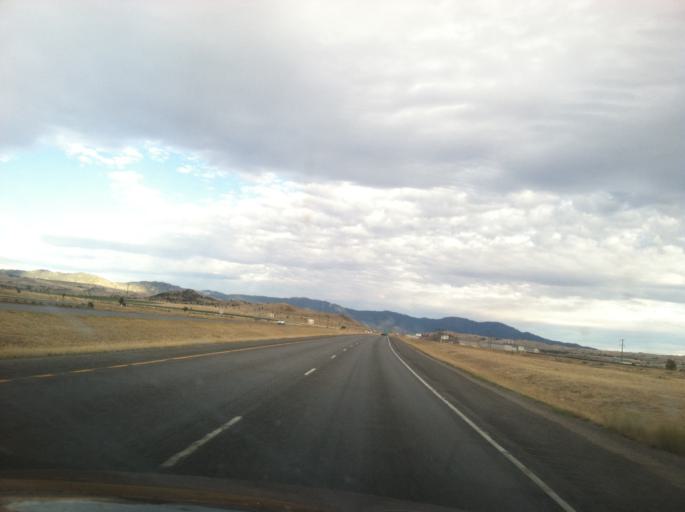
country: US
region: Montana
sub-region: Silver Bow County
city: Butte-Silver Bow (Balance)
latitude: 46.0098
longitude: -112.6844
